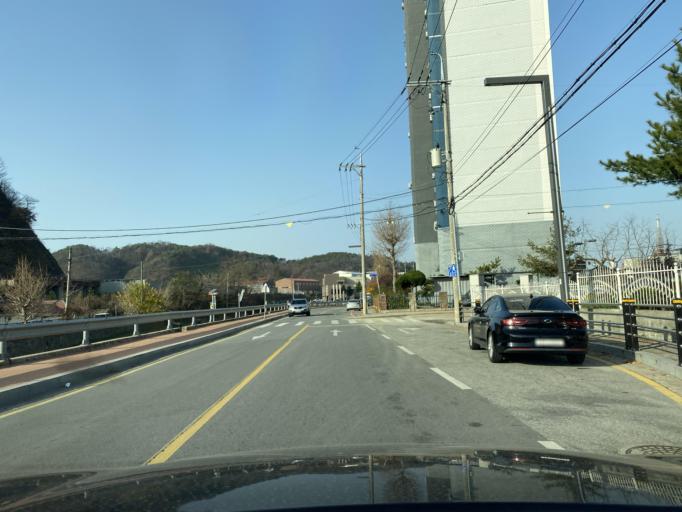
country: KR
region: Chungcheongnam-do
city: Yesan
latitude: 36.6781
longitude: 126.8385
